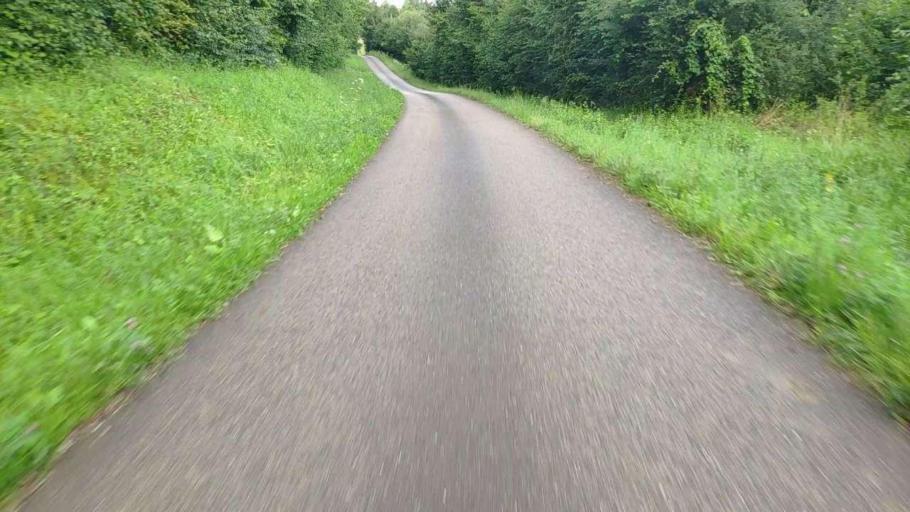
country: FR
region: Franche-Comte
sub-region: Departement du Jura
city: Poligny
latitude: 46.8007
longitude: 5.5950
